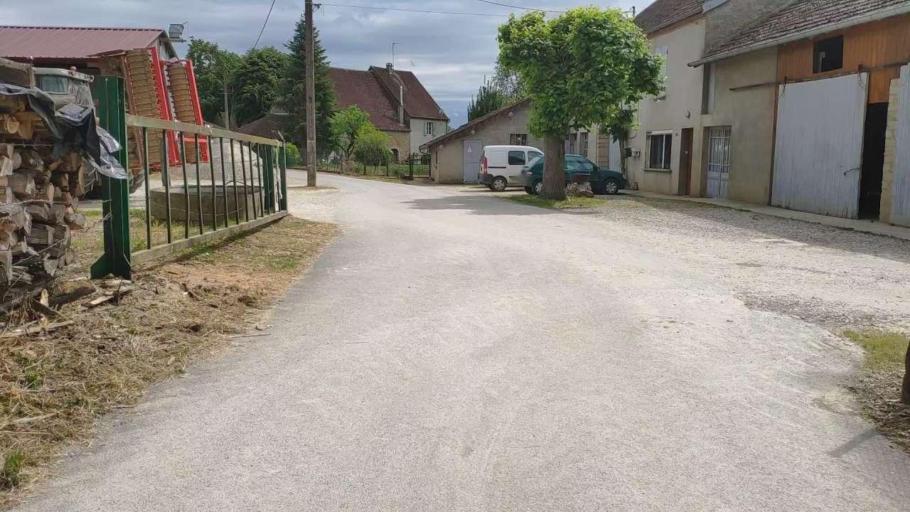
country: FR
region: Franche-Comte
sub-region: Departement du Jura
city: Bletterans
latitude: 46.7387
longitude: 5.4977
